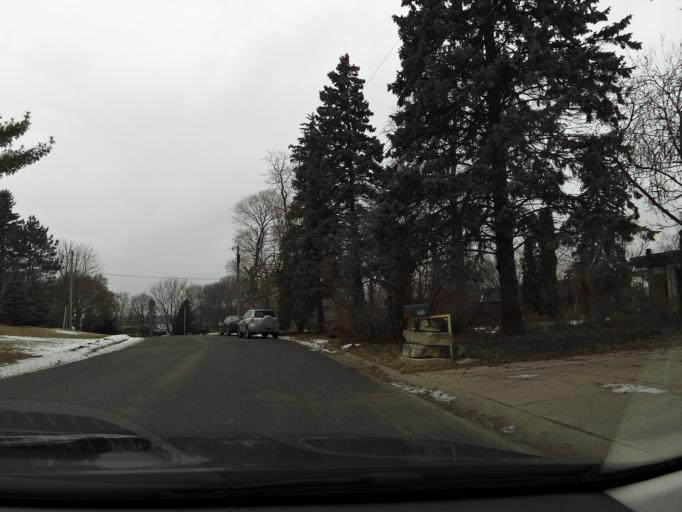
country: US
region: Minnesota
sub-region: Carver County
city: Waconia
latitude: 44.8608
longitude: -93.7967
